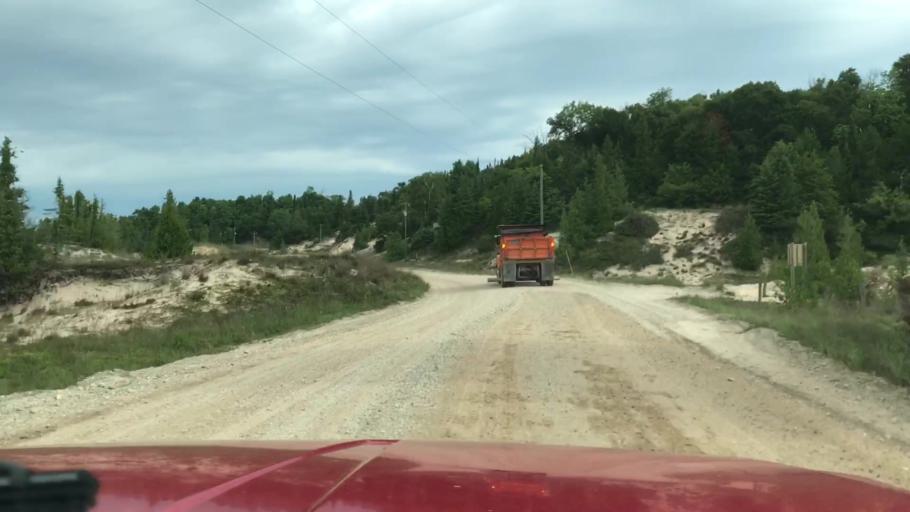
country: US
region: Michigan
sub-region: Charlevoix County
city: Charlevoix
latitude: 45.7380
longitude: -85.5594
